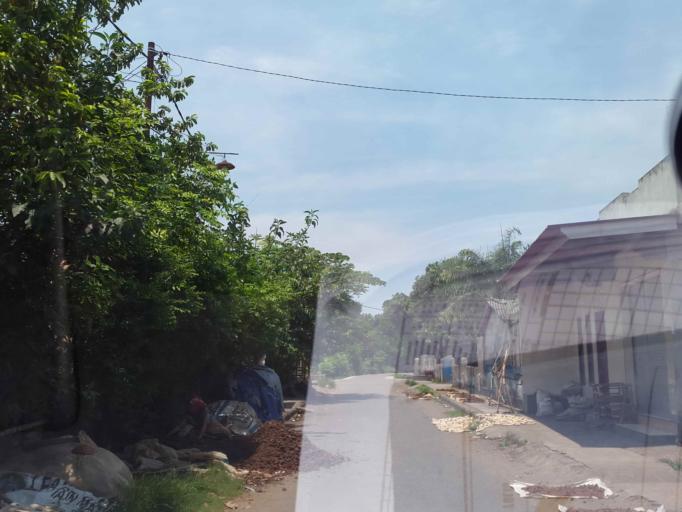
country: ID
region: West Nusa Tenggara
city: Karangkebon Timur
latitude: -8.6475
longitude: 116.1079
